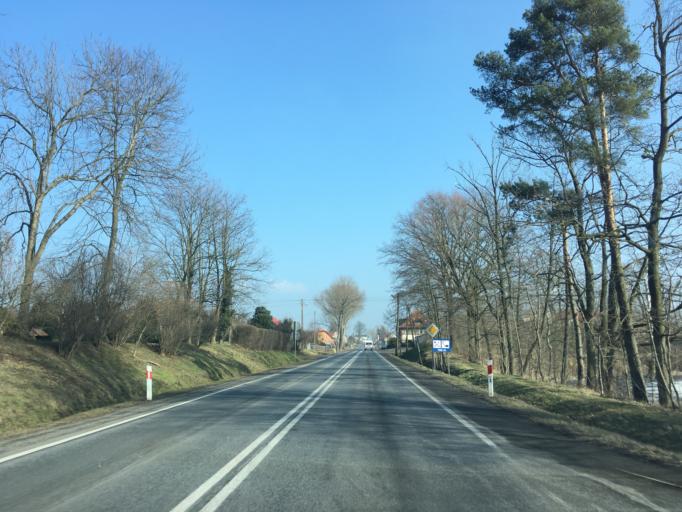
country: PL
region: Lower Silesian Voivodeship
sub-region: Powiat zlotoryjski
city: Olszanica
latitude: 51.2759
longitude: 15.8092
